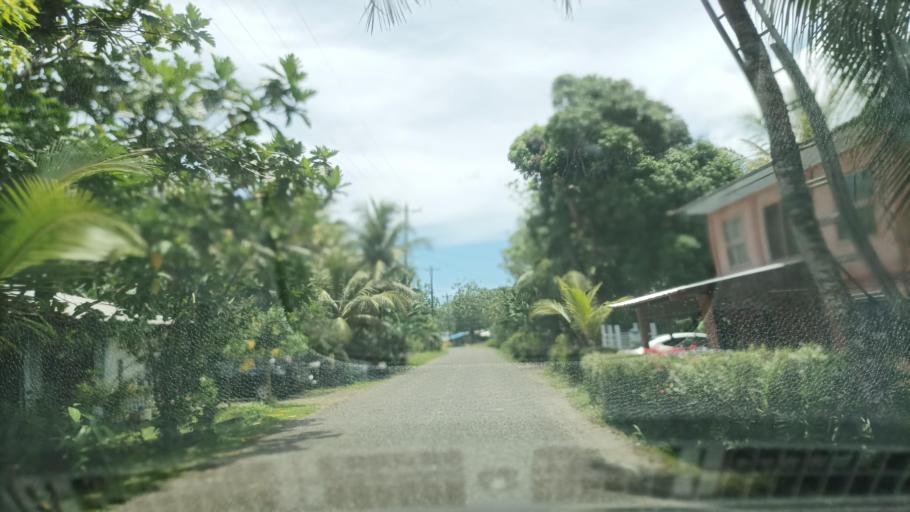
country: FM
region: Kosrae
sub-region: Malem Municipality
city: Malem
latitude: 5.2893
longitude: 163.0278
